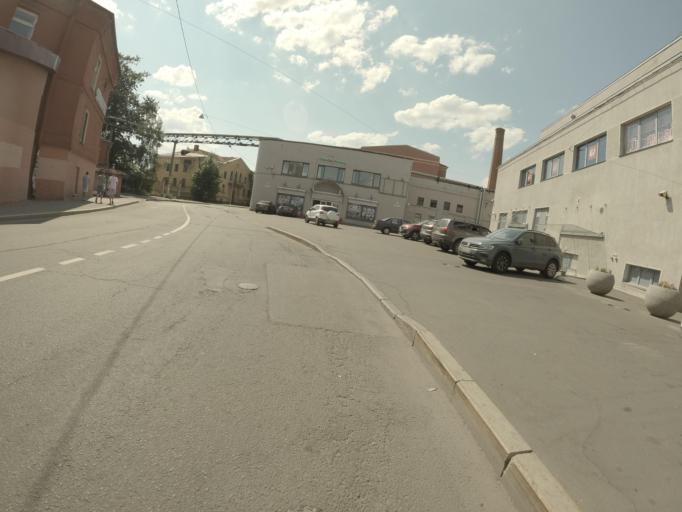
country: RU
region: St.-Petersburg
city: Admiralteisky
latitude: 59.8995
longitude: 30.2727
